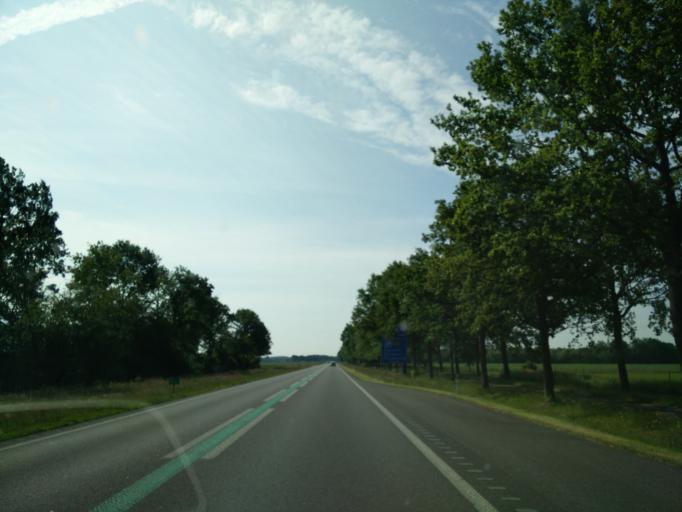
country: NL
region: Drenthe
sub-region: Gemeente Borger-Odoorn
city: Borger
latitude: 52.9841
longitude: 6.7687
